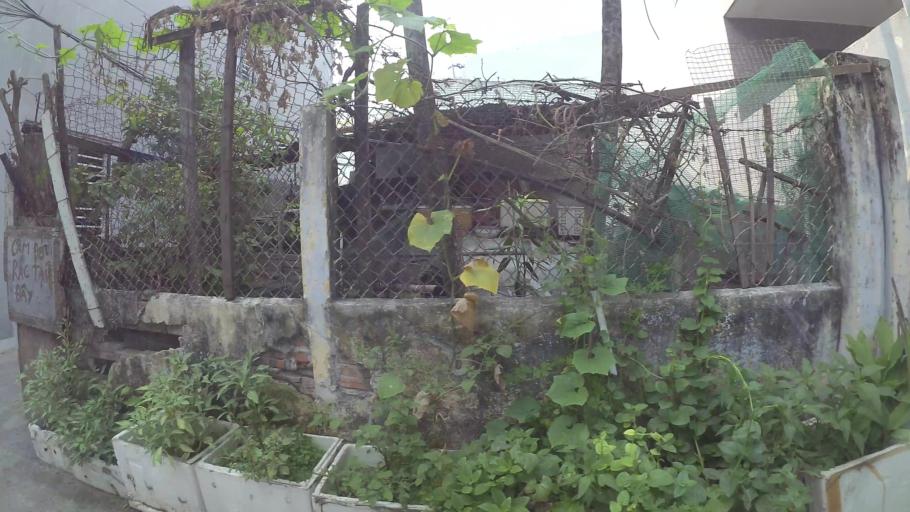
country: VN
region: Da Nang
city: Son Tra
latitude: 16.0437
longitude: 108.2155
